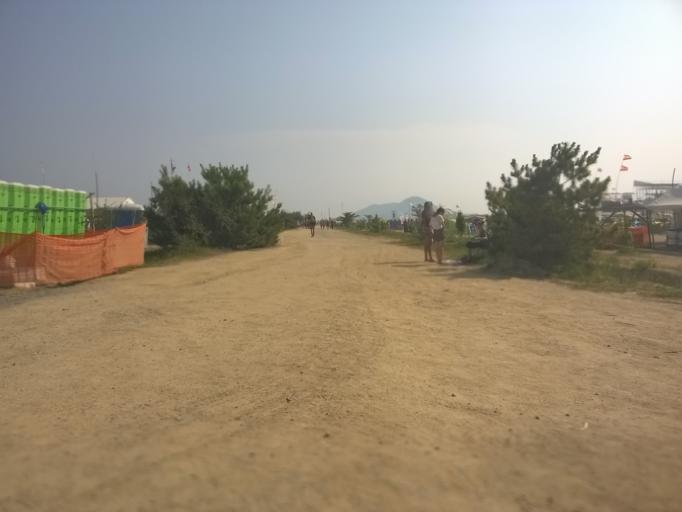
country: JP
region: Yamaguchi
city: Ogori-shimogo
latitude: 34.0212
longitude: 131.3736
